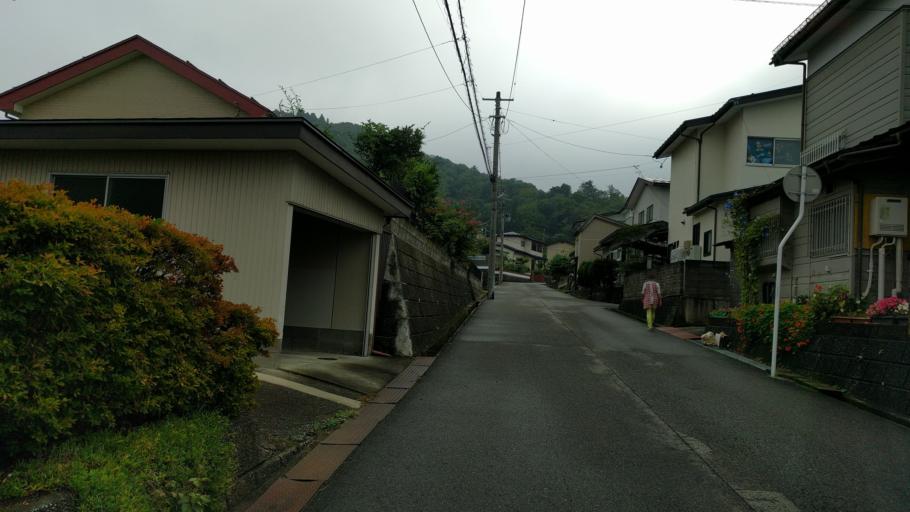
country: JP
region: Fukushima
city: Kitakata
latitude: 37.5029
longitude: 139.9498
